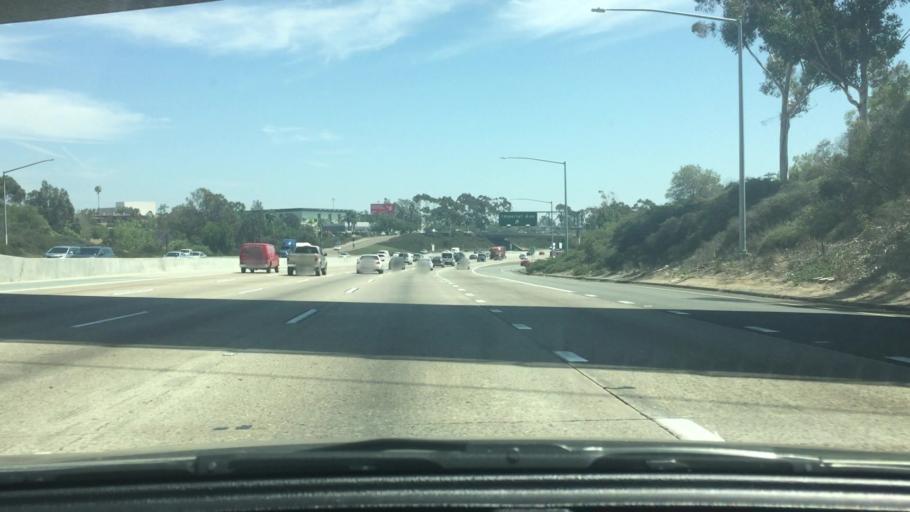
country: US
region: California
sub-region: San Diego County
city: National City
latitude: 32.7077
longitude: -117.0974
